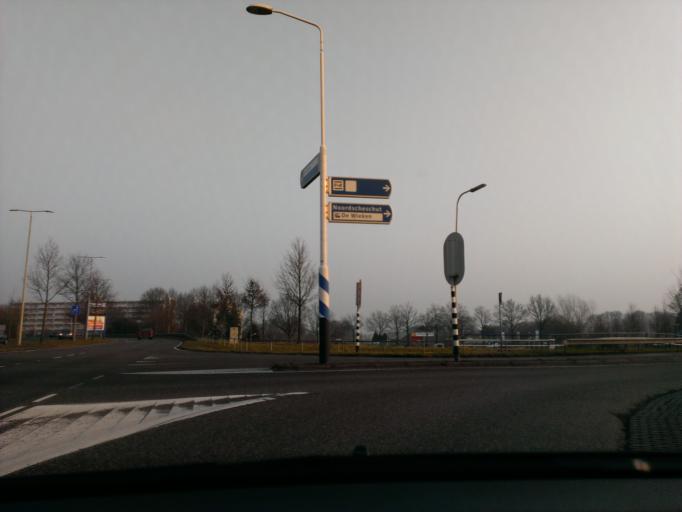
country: NL
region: Drenthe
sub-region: Gemeente Hoogeveen
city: Hoogeveen
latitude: 52.7176
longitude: 6.5176
